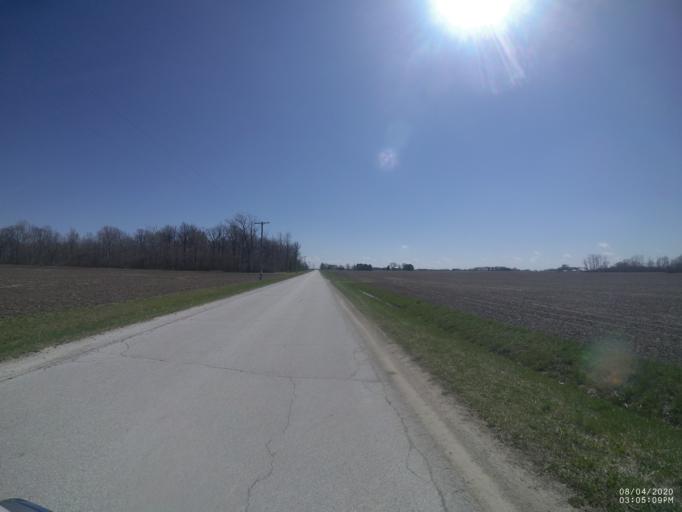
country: US
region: Ohio
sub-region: Sandusky County
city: Stony Prairie
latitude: 41.3098
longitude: -83.2405
